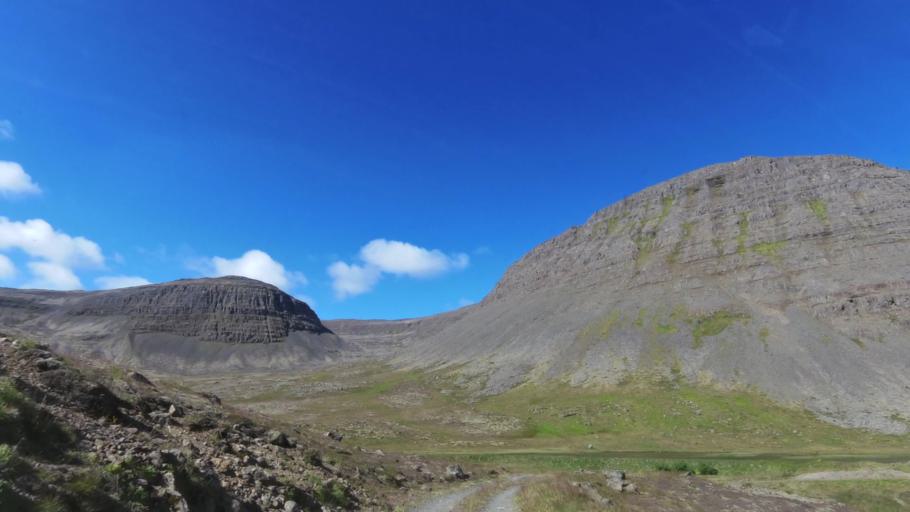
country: IS
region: West
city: Olafsvik
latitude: 65.6246
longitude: -23.8935
